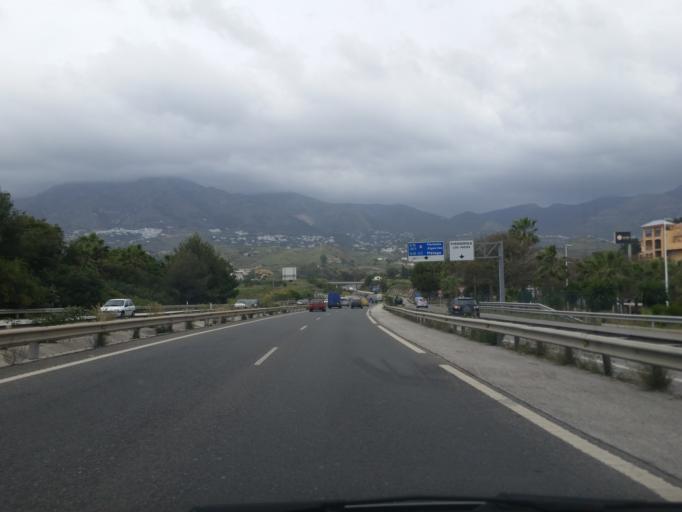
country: ES
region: Andalusia
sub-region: Provincia de Malaga
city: Fuengirola
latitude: 36.5620
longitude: -4.6213
